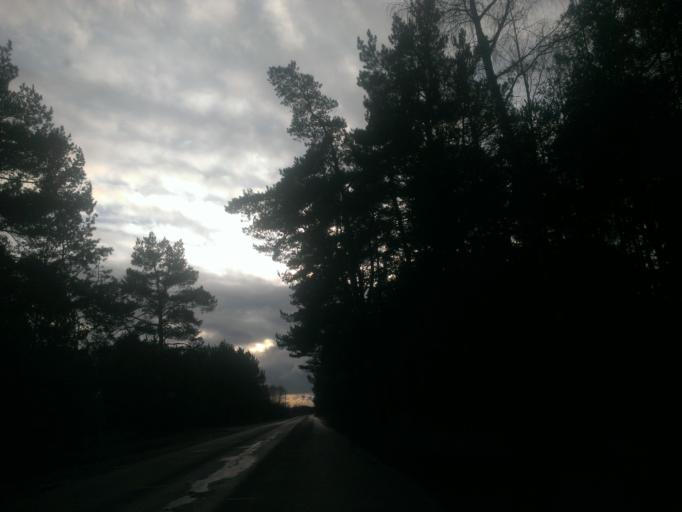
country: LV
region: Riga
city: Bolderaja
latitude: 57.0692
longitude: 24.0882
